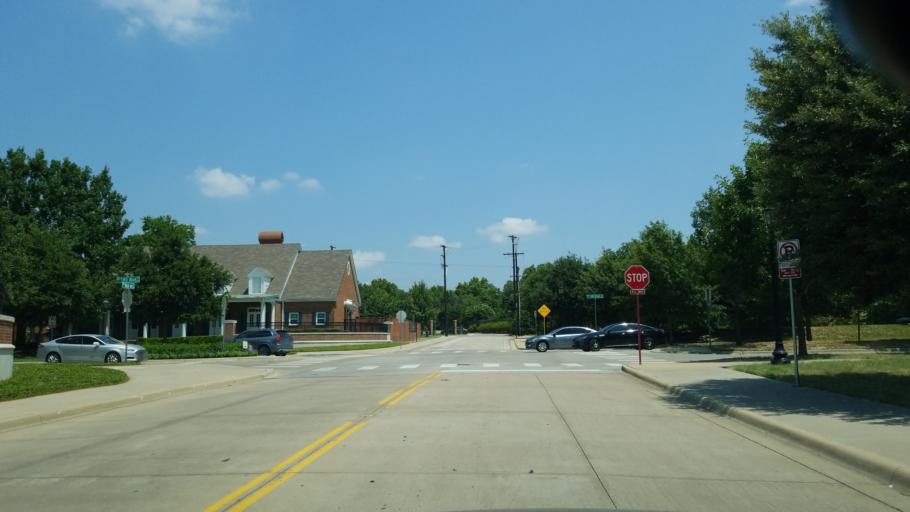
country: US
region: Texas
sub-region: Dallas County
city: Highland Park
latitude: 32.8417
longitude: -96.7794
